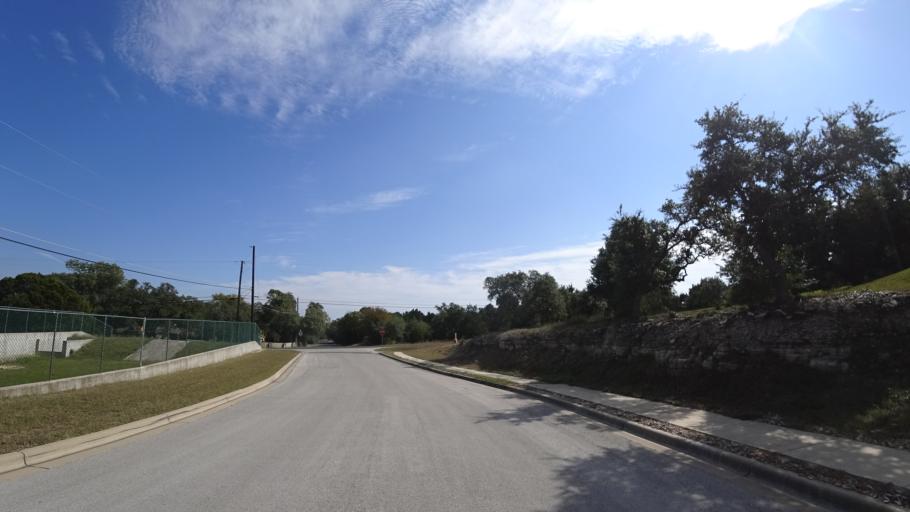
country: US
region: Texas
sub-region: Travis County
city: Bee Cave
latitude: 30.2265
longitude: -97.9301
